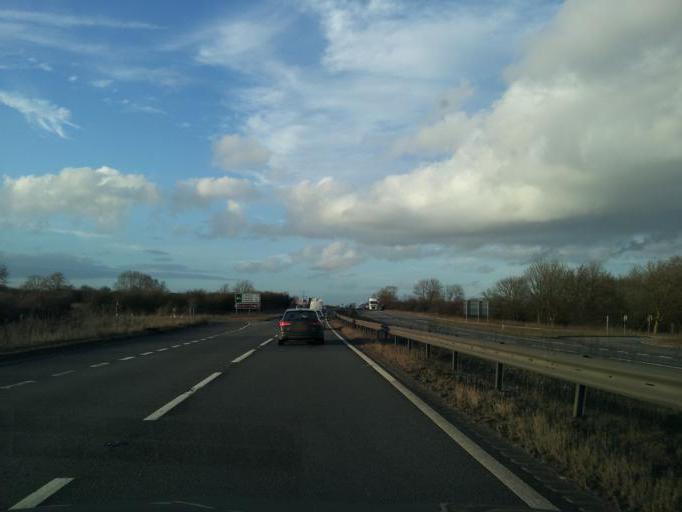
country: GB
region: England
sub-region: District of Rutland
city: Greetham
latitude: 52.7604
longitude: -0.6100
